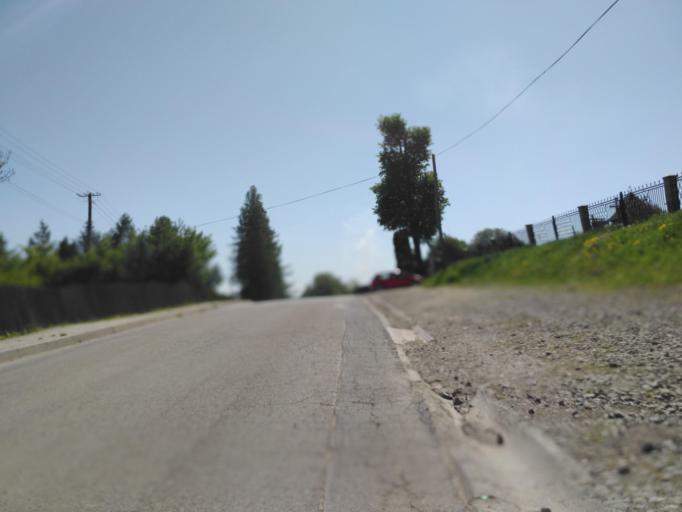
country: PL
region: Subcarpathian Voivodeship
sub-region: Powiat krosnienski
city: Miejsce Piastowe
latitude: 49.6119
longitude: 21.7582
